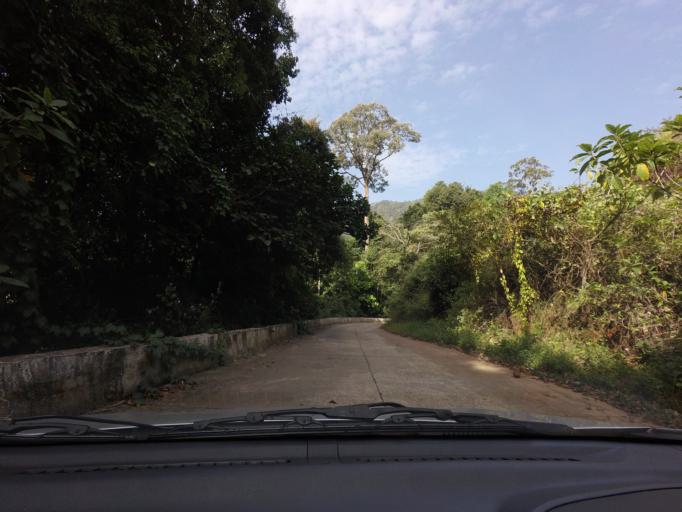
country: IN
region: Karnataka
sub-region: Kodagu
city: Sanivarsante
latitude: 12.7276
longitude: 75.6621
